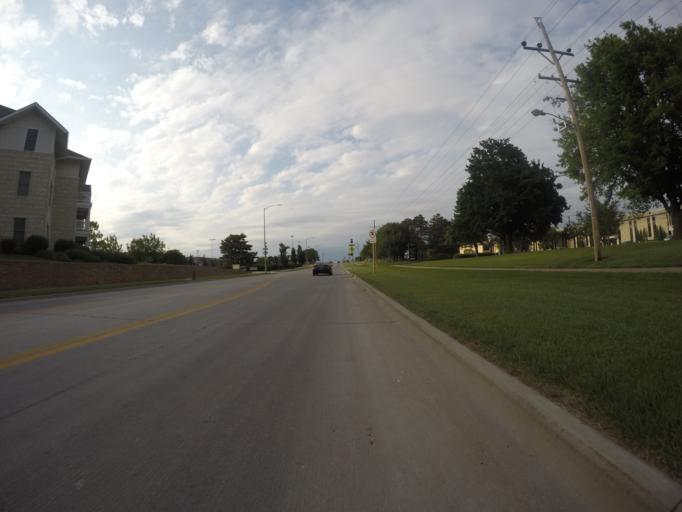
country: US
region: Kansas
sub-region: Riley County
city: Manhattan
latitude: 39.1985
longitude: -96.5854
